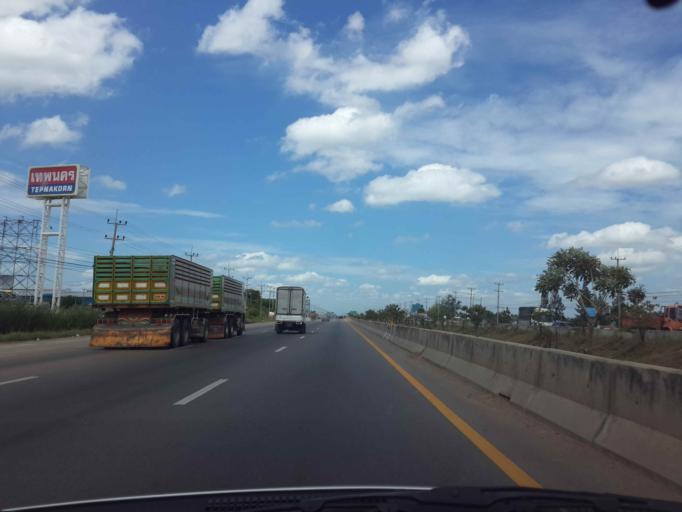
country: TH
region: Samut Songkhram
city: Samut Songkhram
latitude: 13.4526
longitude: 100.0840
